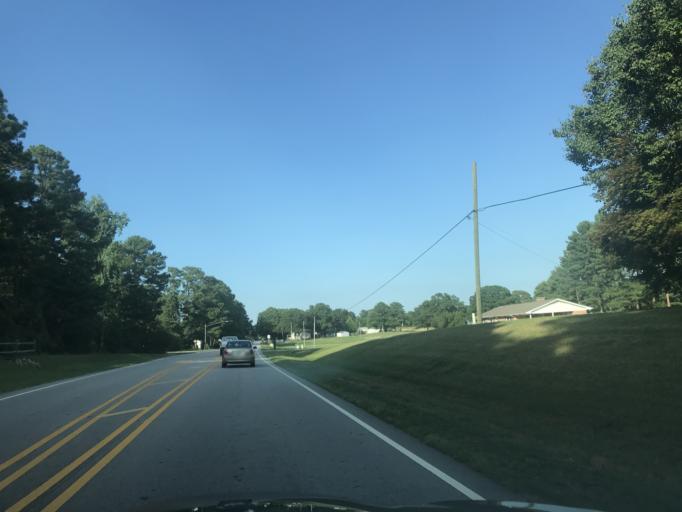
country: US
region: North Carolina
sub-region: Wake County
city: Rolesville
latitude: 35.9292
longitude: -78.4488
